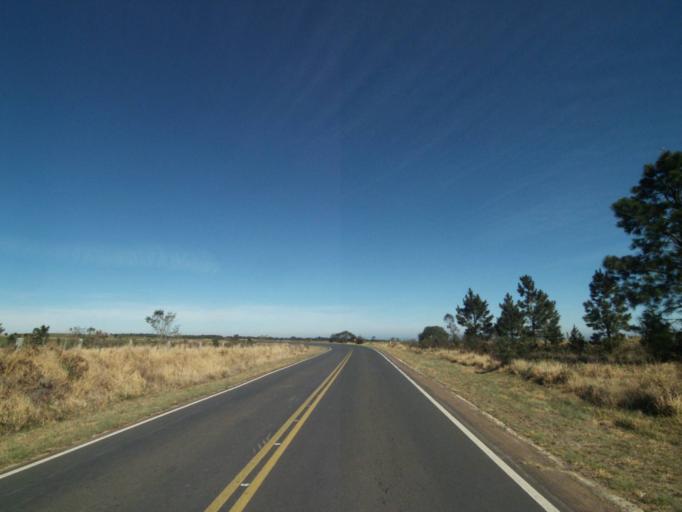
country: BR
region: Parana
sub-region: Tibagi
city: Tibagi
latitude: -24.6409
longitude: -50.2329
